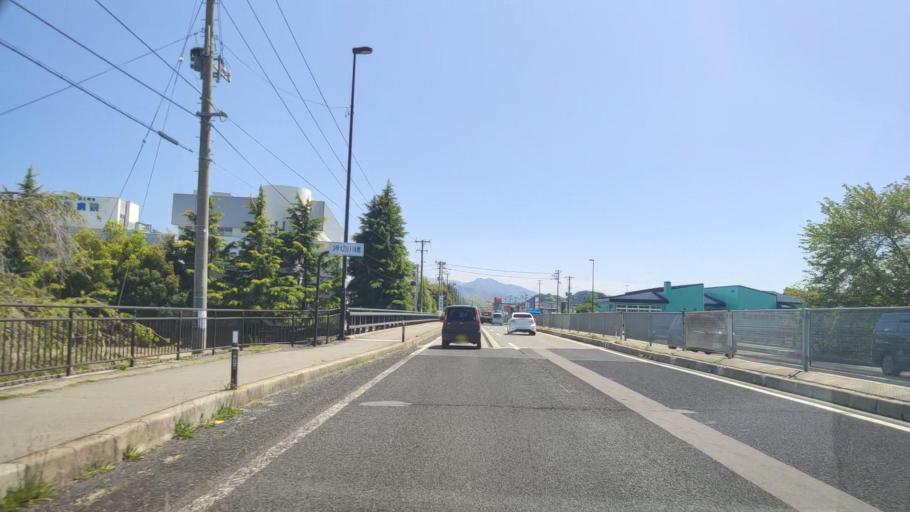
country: JP
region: Yamagata
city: Tendo
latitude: 38.3823
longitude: 140.3822
